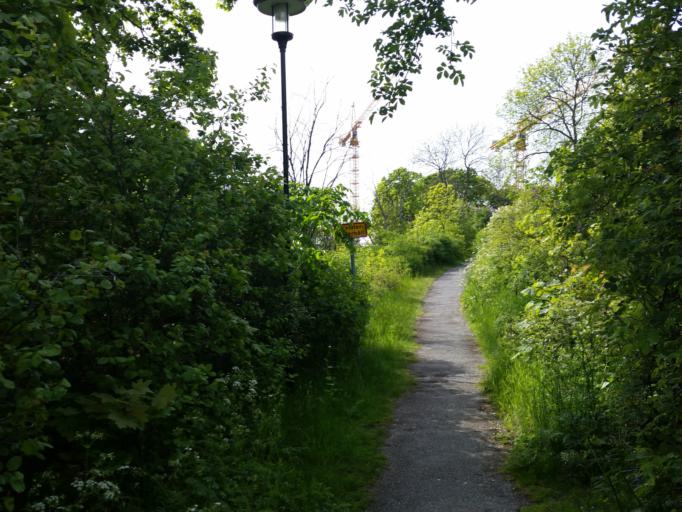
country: SE
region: Stockholm
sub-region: Stockholms Kommun
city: Arsta
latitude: 59.3106
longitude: 18.0264
